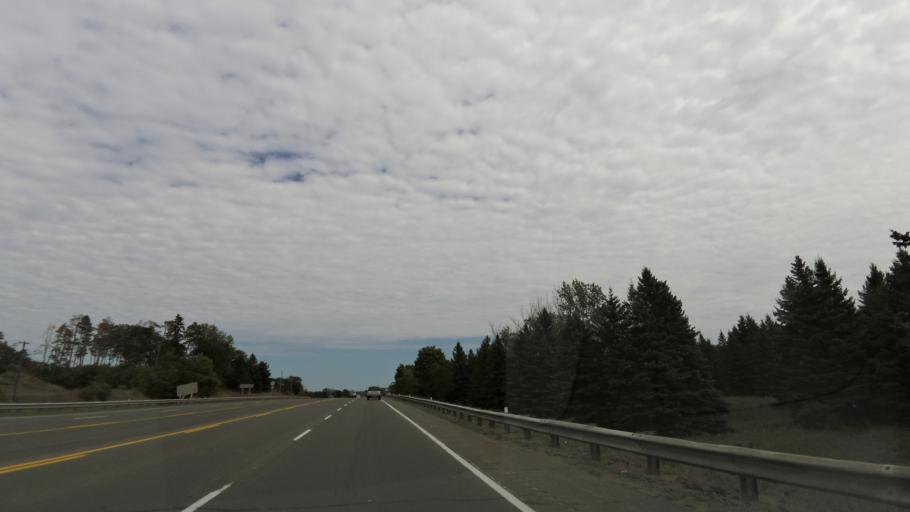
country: CA
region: Ontario
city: Bradford West Gwillimbury
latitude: 44.0323
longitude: -79.5783
